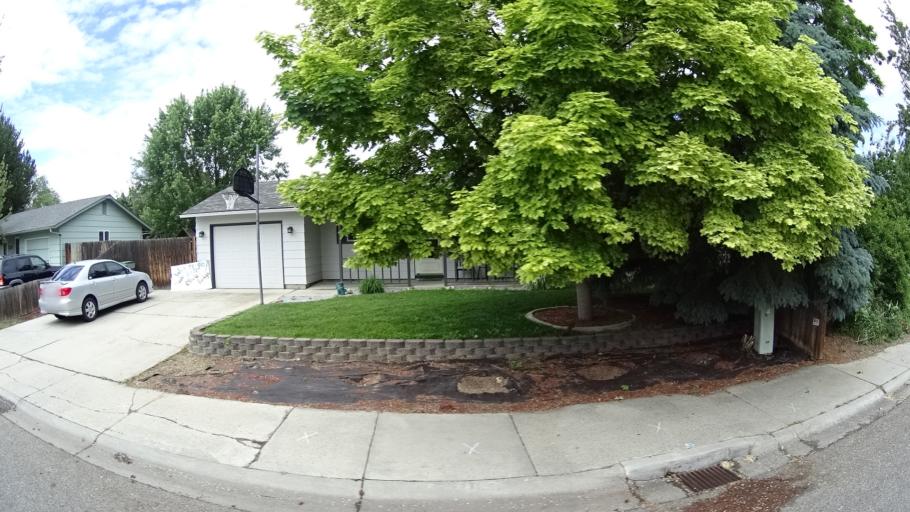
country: US
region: Idaho
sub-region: Ada County
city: Boise
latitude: 43.5732
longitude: -116.1635
